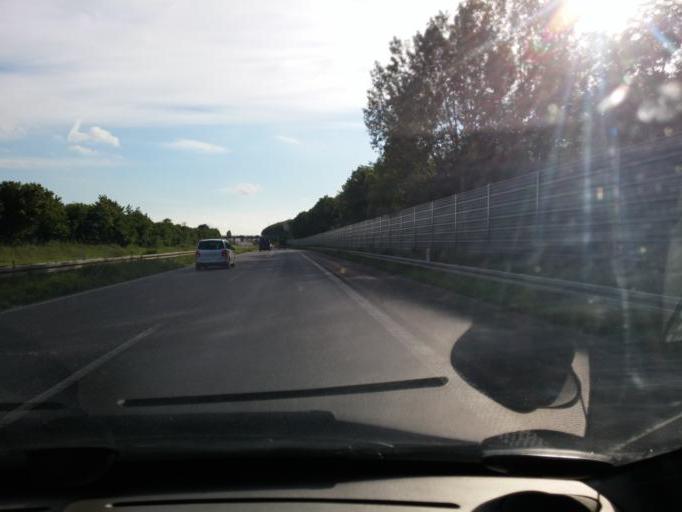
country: DK
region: Zealand
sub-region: Slagelse Kommune
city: Slagelse
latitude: 55.3869
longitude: 11.3466
